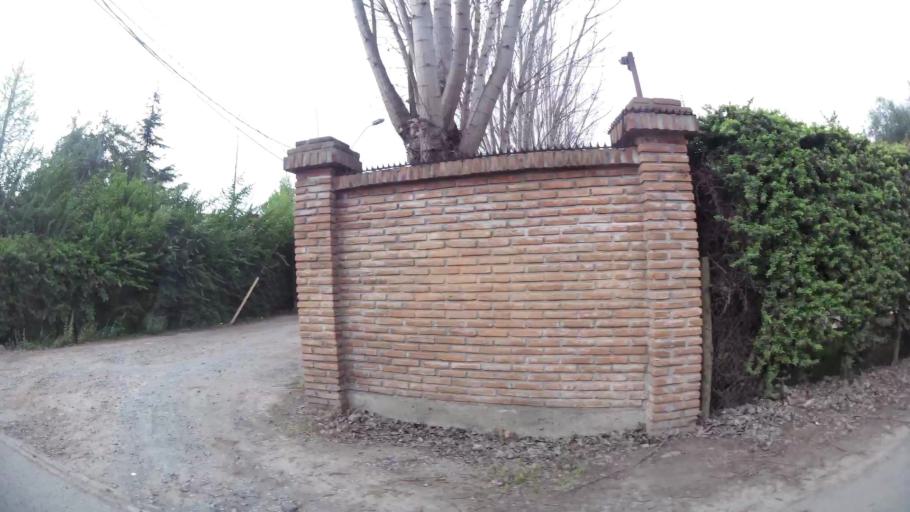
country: CL
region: Santiago Metropolitan
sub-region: Provincia de Chacabuco
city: Chicureo Abajo
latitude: -33.2609
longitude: -70.7093
